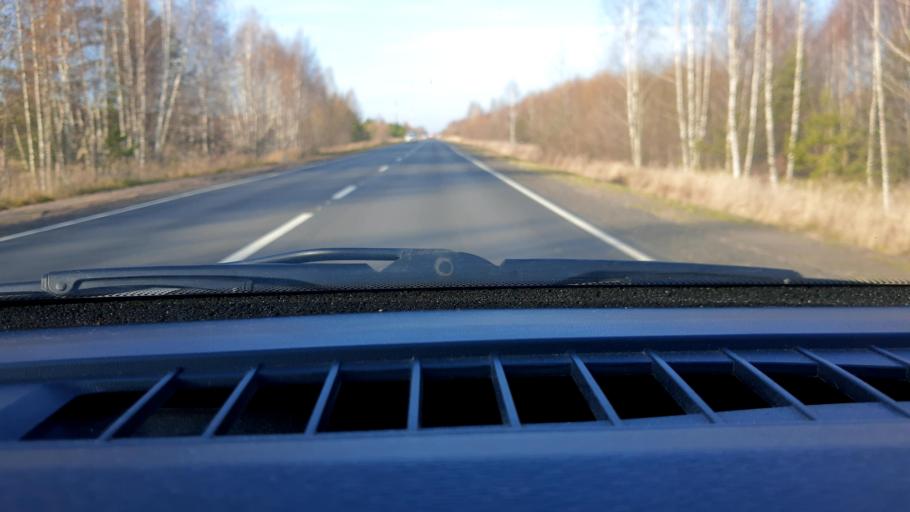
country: RU
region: Nizjnij Novgorod
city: Novaya Balakhna
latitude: 56.5916
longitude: 43.6586
